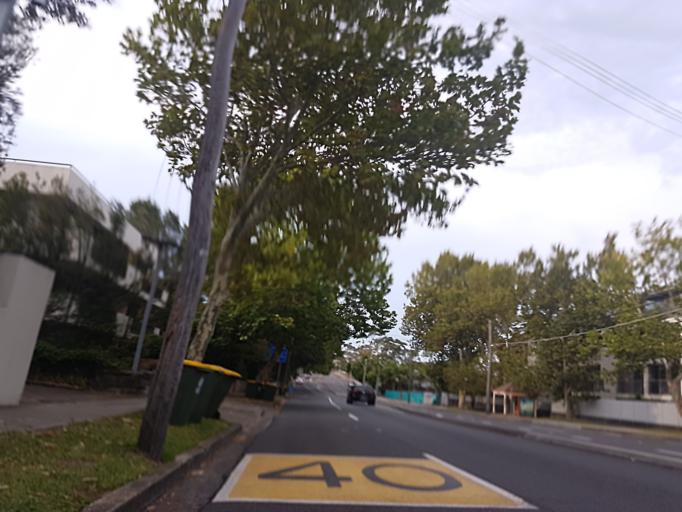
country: AU
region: New South Wales
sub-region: North Sydney
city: Crows Nest
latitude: -33.8266
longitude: 151.2094
